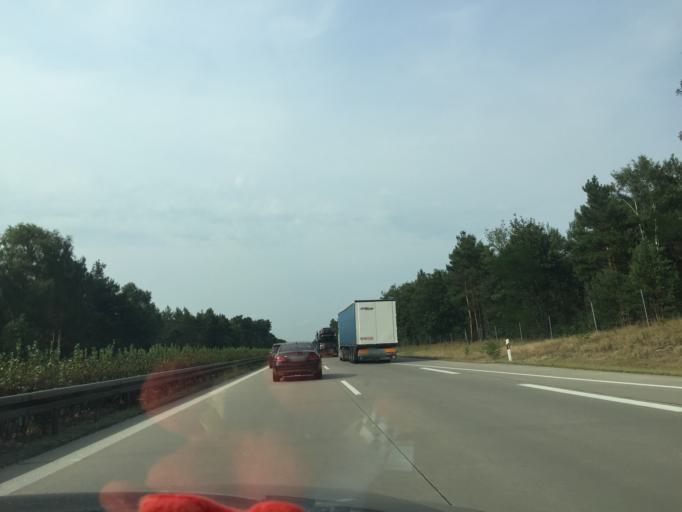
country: DE
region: Brandenburg
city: Halbe
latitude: 52.0662
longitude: 13.6523
